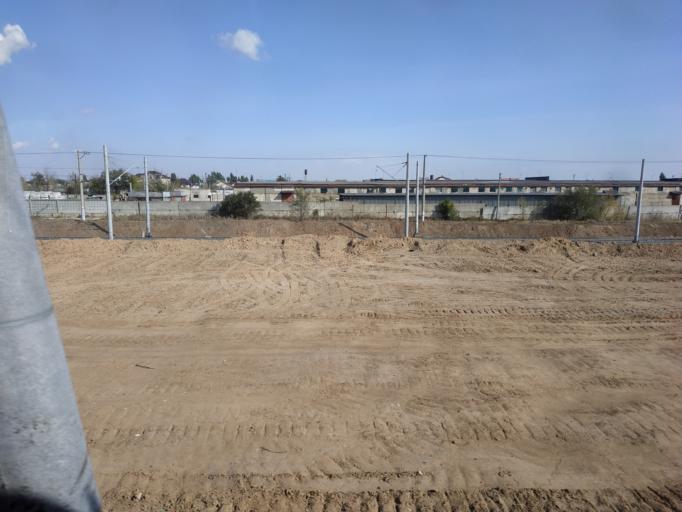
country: RU
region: Volgograd
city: Gumrak
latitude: 48.7723
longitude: 44.3856
